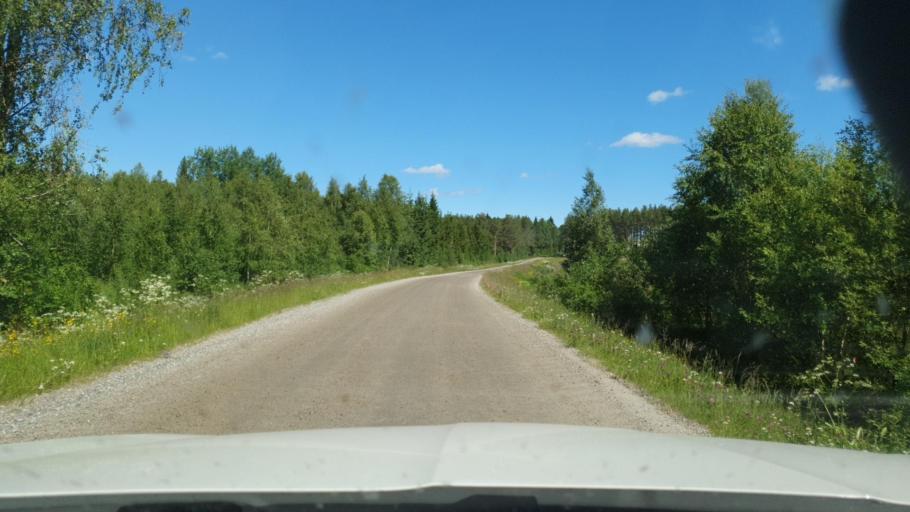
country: SE
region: Vaesterbotten
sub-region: Skelleftea Kommun
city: Byske
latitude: 65.1115
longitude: 21.1966
